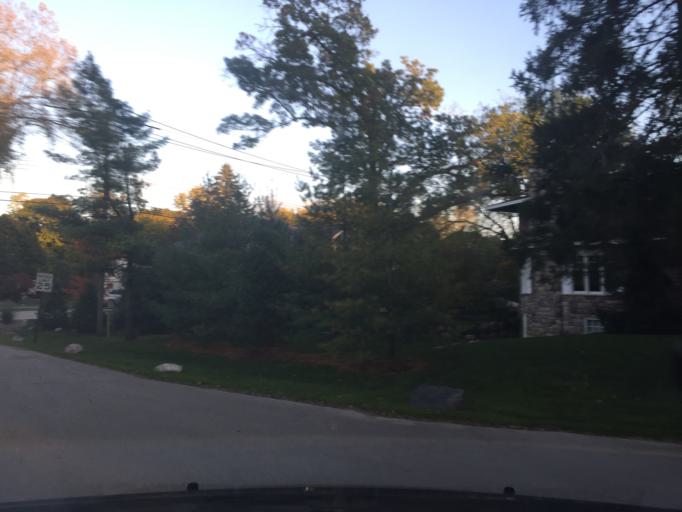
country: US
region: Michigan
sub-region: Oakland County
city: Franklin
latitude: 42.5489
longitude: -83.2935
